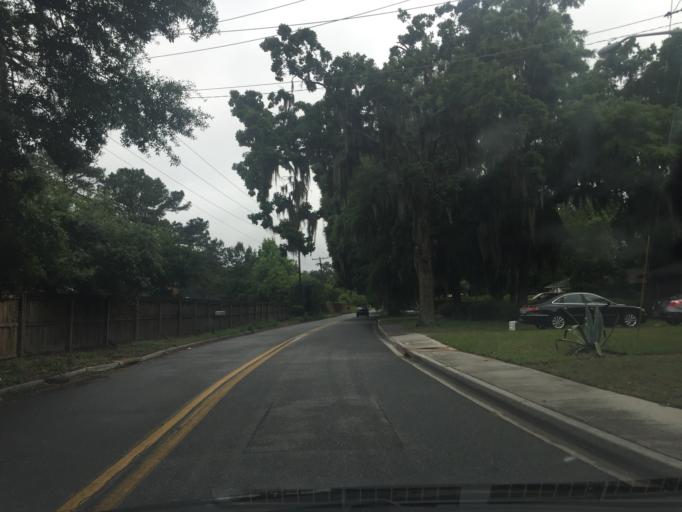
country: US
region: Georgia
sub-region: Chatham County
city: Isle of Hope
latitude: 31.9900
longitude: -81.0954
